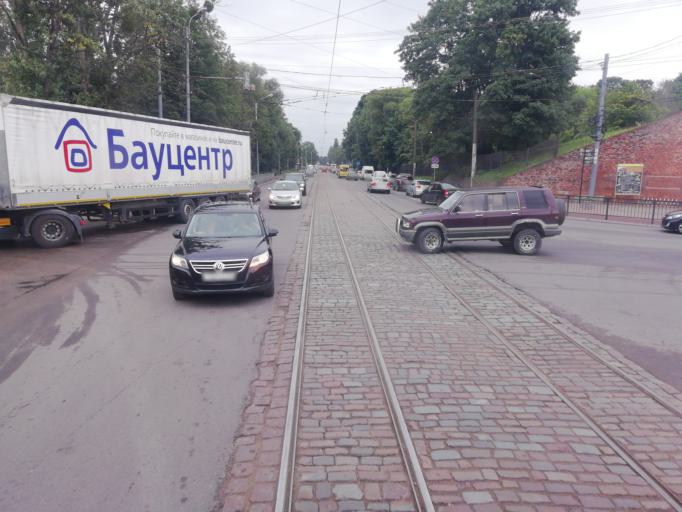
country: RU
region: Kaliningrad
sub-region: Gorod Kaliningrad
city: Kaliningrad
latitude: 54.6958
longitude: 20.5218
